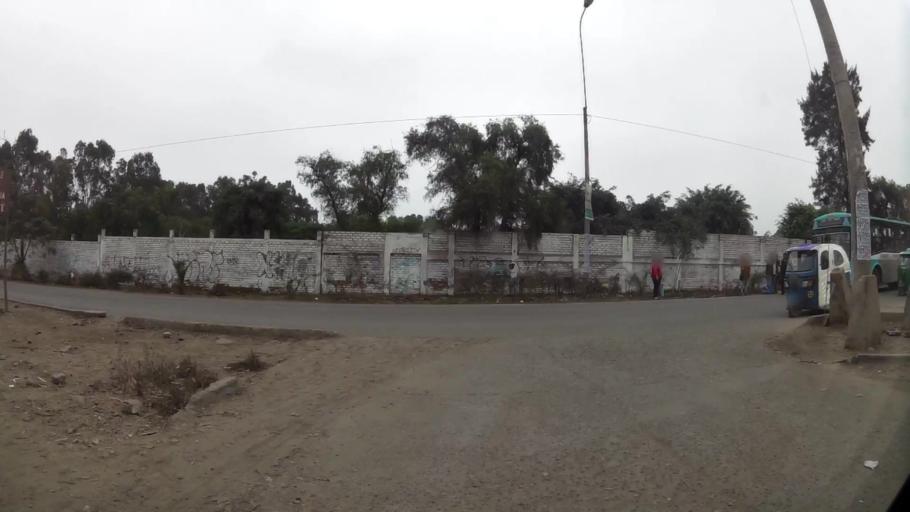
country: PE
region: Lima
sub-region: Lima
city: Surco
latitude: -12.2323
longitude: -76.9253
